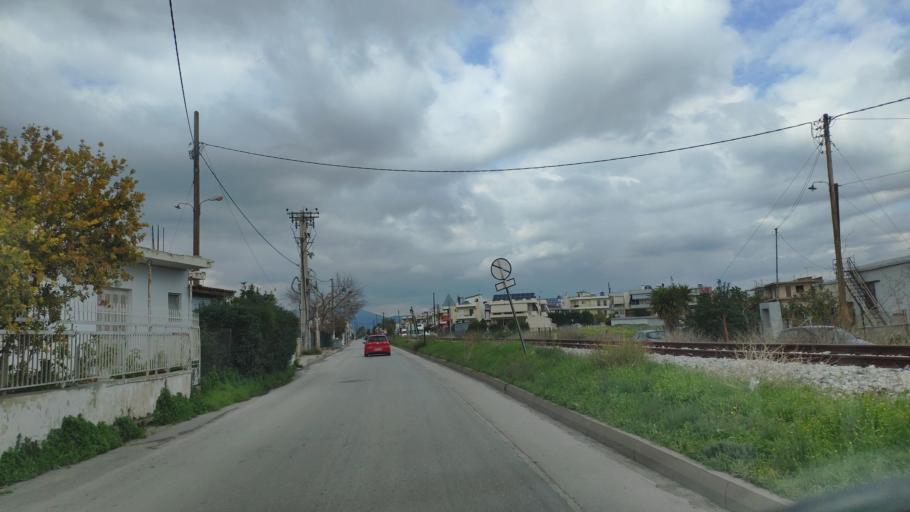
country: GR
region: Peloponnese
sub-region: Nomos Argolidos
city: Argos
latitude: 37.6377
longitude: 22.7345
